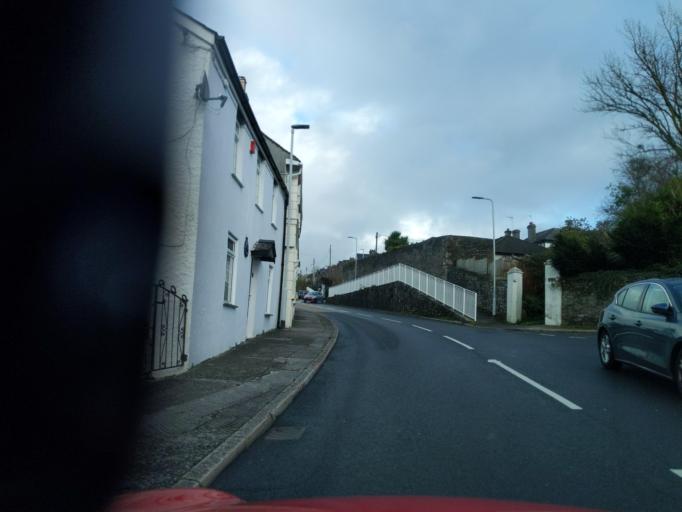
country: GB
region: England
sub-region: Plymouth
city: Plymouth
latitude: 50.4298
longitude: -4.1546
